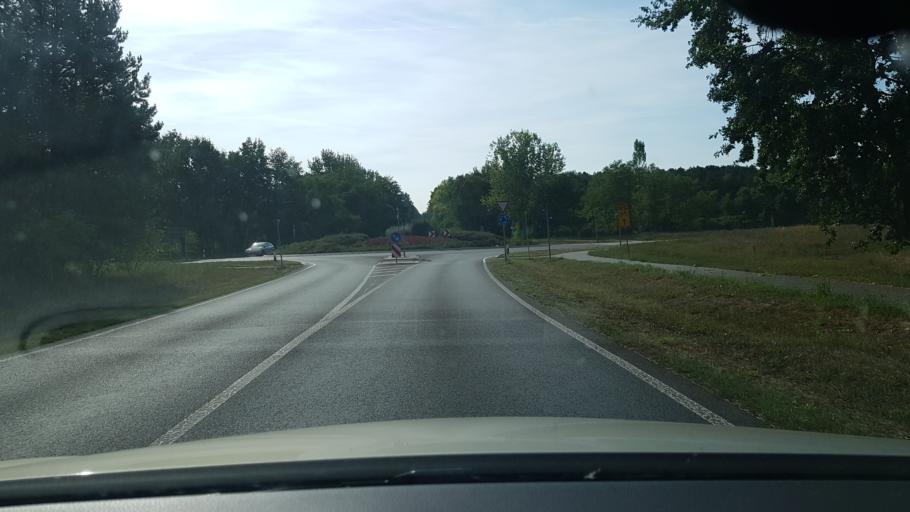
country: DE
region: Brandenburg
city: Lawitz
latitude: 52.1239
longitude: 14.6413
